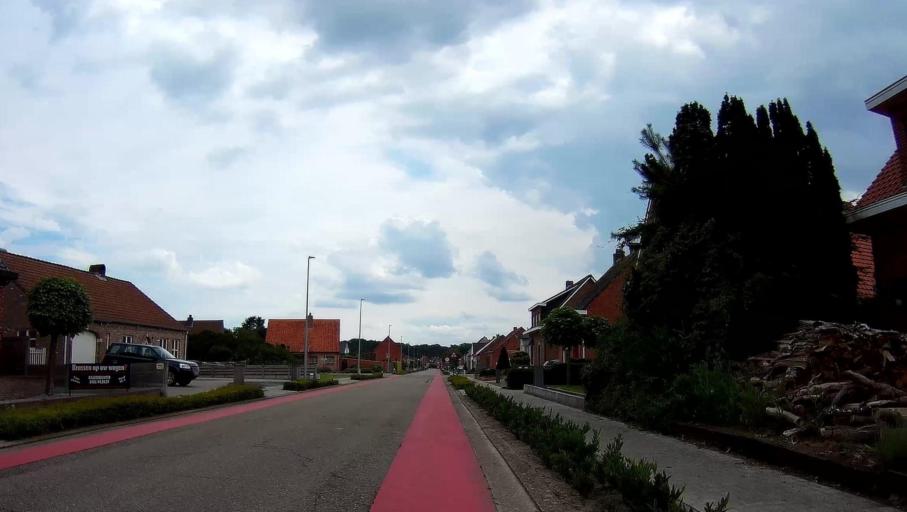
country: BE
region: Flanders
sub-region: Provincie Antwerpen
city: Dessel
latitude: 51.2394
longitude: 5.1565
